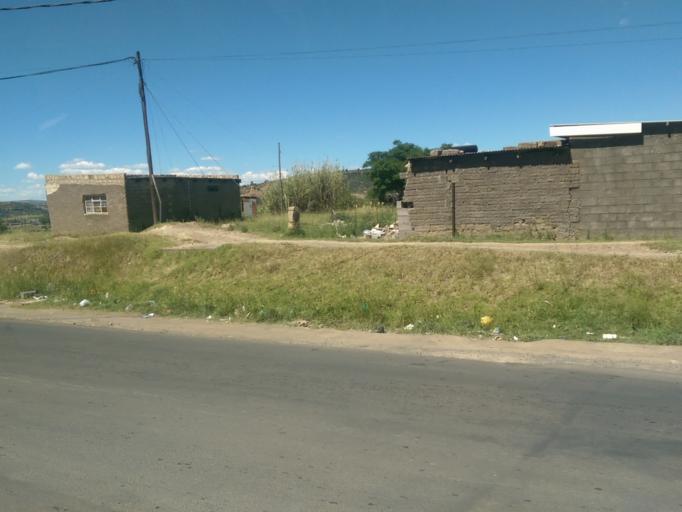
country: LS
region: Maseru
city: Maseru
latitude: -29.4128
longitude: 27.5582
